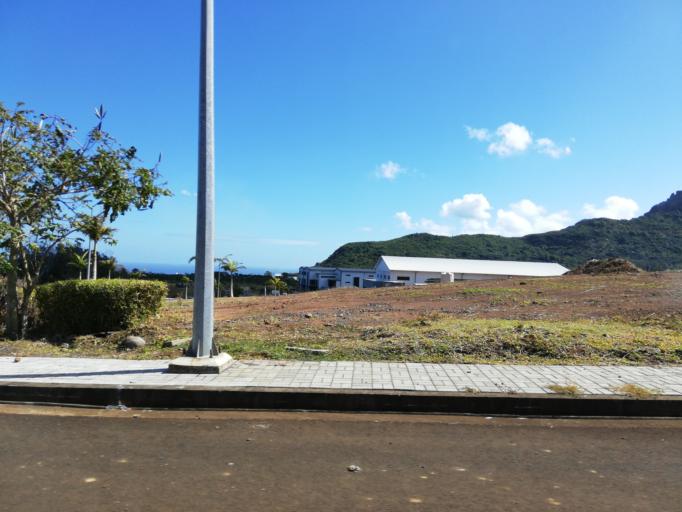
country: MU
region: Moka
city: Moka
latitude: -20.2249
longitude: 57.4909
